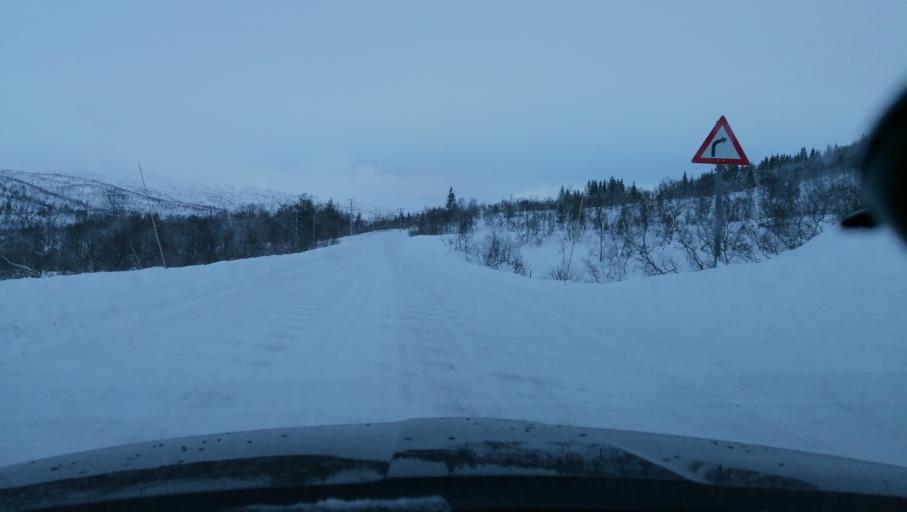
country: NO
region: Aust-Agder
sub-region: Bykle
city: Hovden
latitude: 59.6368
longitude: 7.4539
